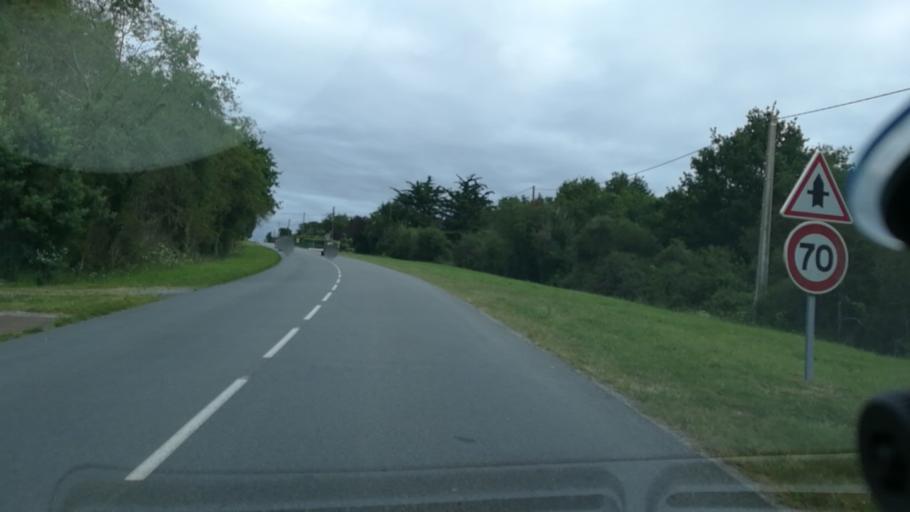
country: FR
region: Brittany
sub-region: Departement du Morbihan
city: Penestin
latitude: 47.4715
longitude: -2.4785
